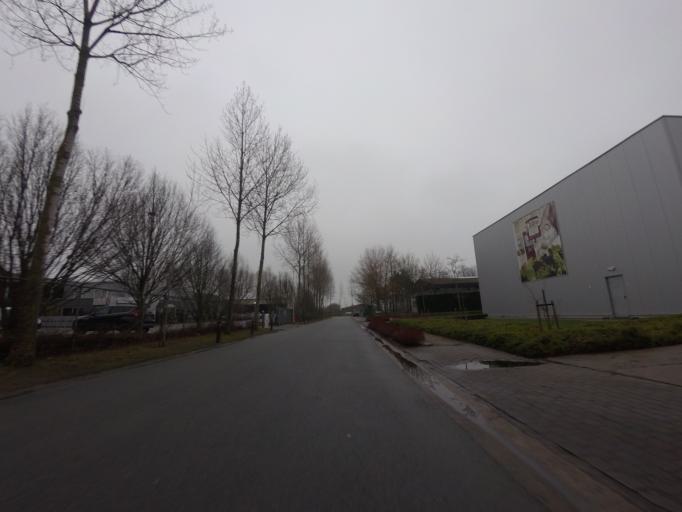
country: BE
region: Flanders
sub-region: Provincie West-Vlaanderen
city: Knokke-Heist
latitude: 51.3216
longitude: 3.2895
